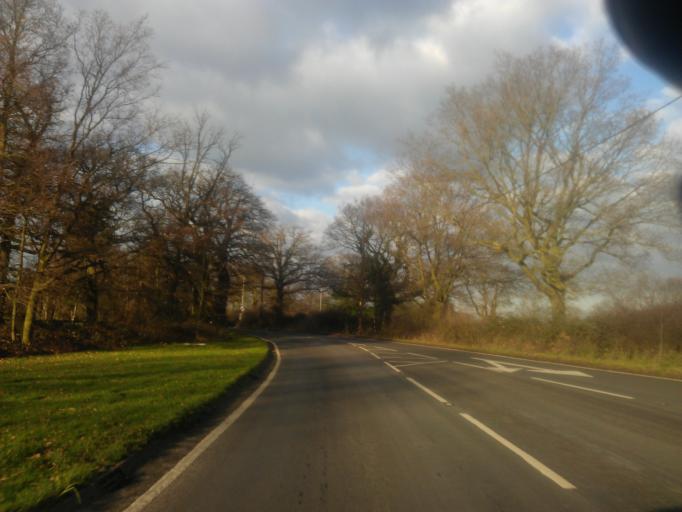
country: GB
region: England
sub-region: Essex
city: Wivenhoe
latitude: 51.8763
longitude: 0.9587
